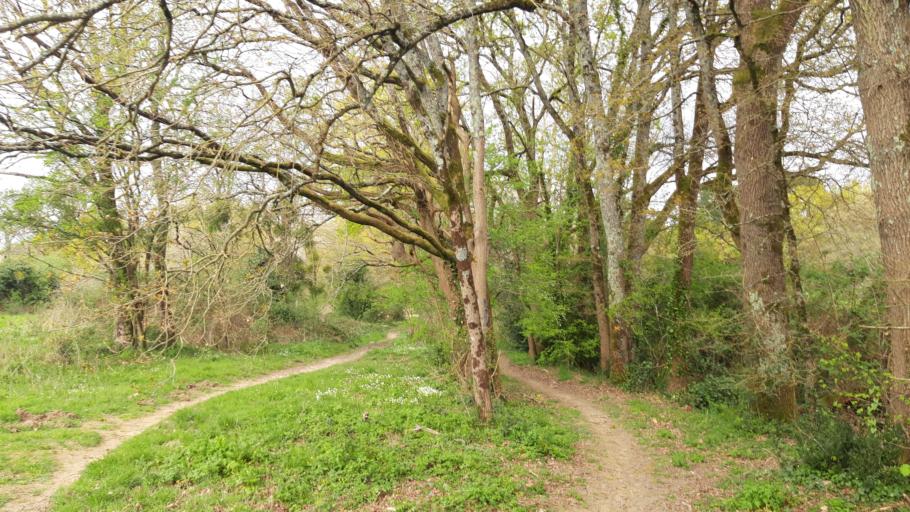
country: FR
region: Pays de la Loire
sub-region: Departement de la Loire-Atlantique
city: Orvault
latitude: 47.2339
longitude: -1.6072
